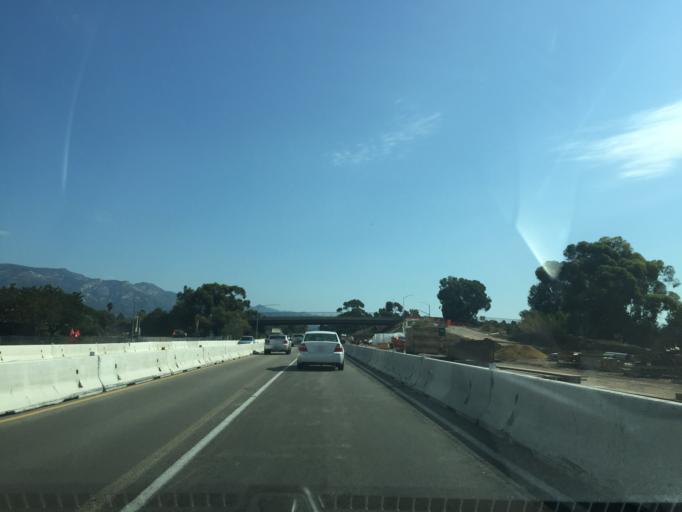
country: US
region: California
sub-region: Santa Barbara County
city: Goleta
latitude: 34.4393
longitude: -119.8353
